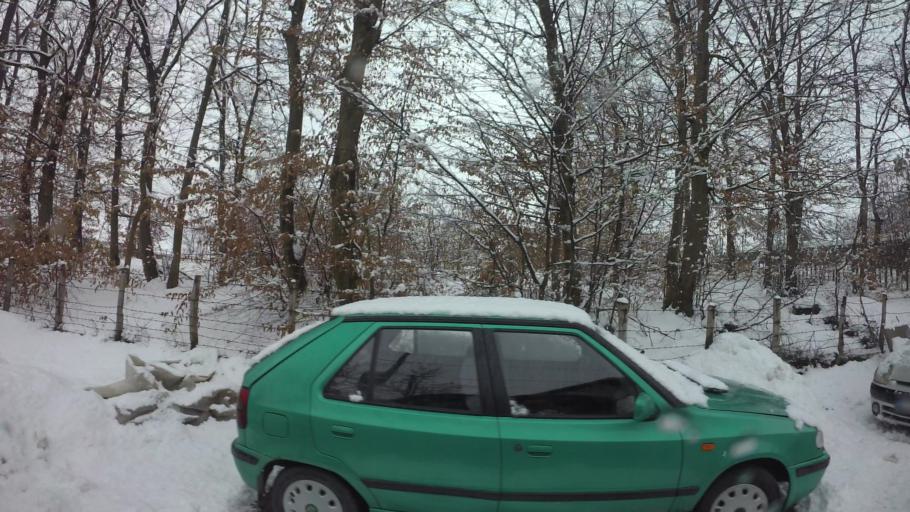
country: BA
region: Federation of Bosnia and Herzegovina
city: Hadzici
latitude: 43.8554
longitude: 18.2608
